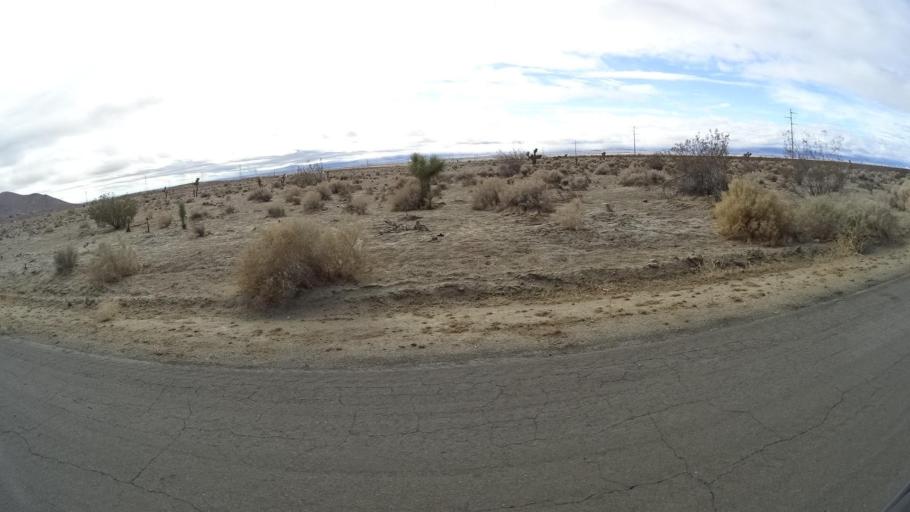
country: US
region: California
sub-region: Kern County
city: Rosamond
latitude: 34.8926
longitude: -118.3108
